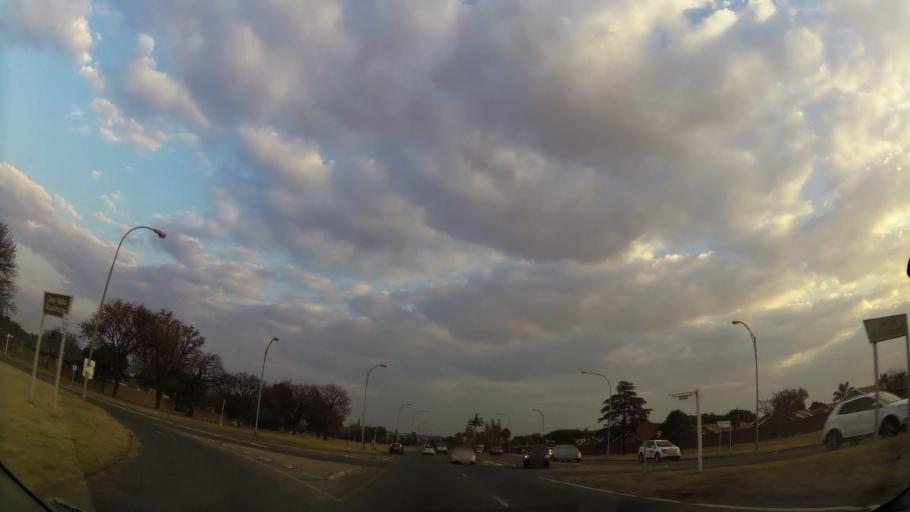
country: ZA
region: Gauteng
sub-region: Ekurhuleni Metropolitan Municipality
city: Benoni
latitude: -26.1718
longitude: 28.3110
